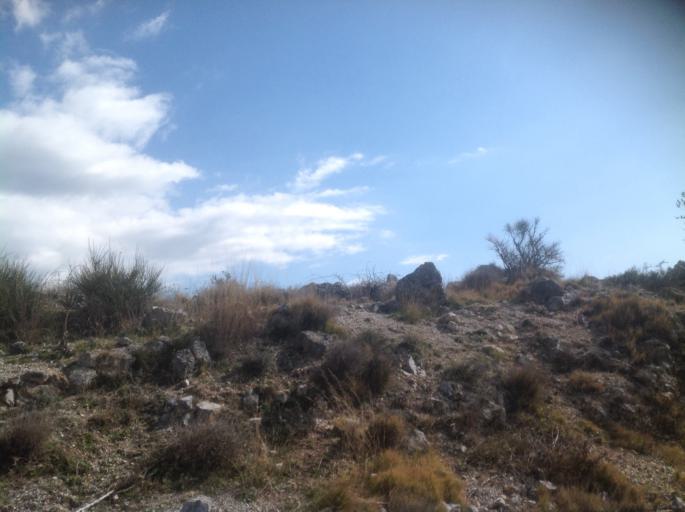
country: IT
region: Calabria
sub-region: Provincia di Cosenza
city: Civita
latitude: 39.8284
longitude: 16.3072
